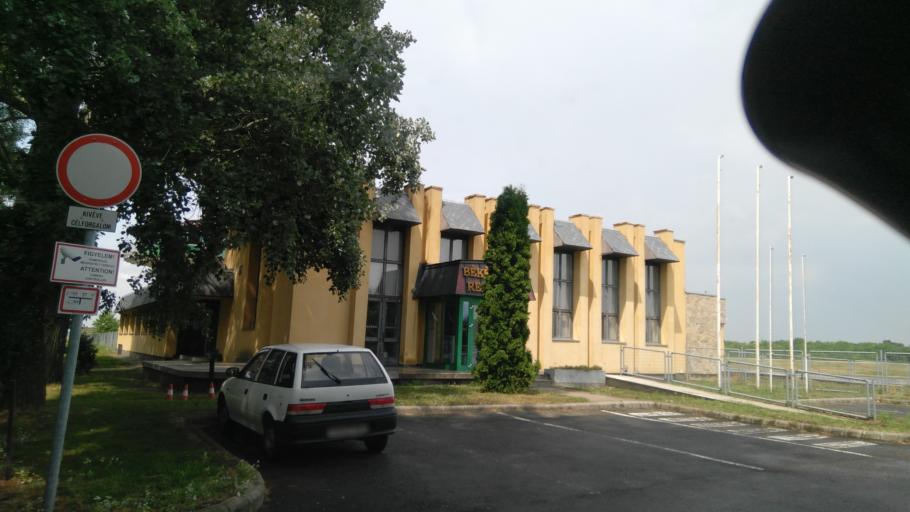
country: HU
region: Bekes
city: Bekescsaba
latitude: 46.6763
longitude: 21.1612
